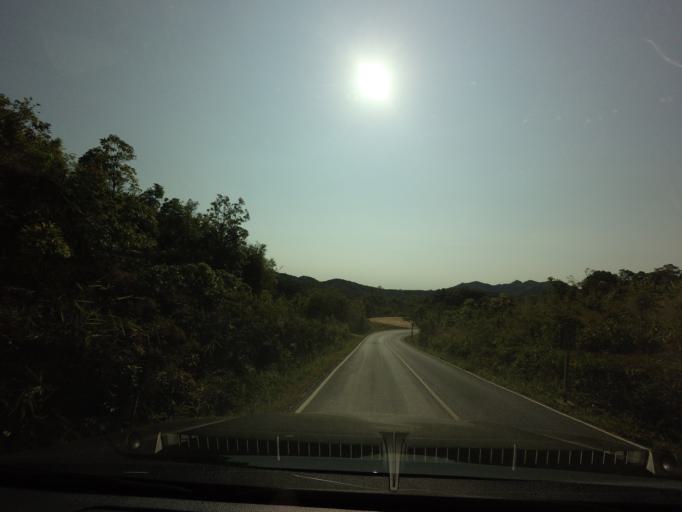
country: TH
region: Kanchanaburi
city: Thong Pha Phum
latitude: 14.6767
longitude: 98.3745
